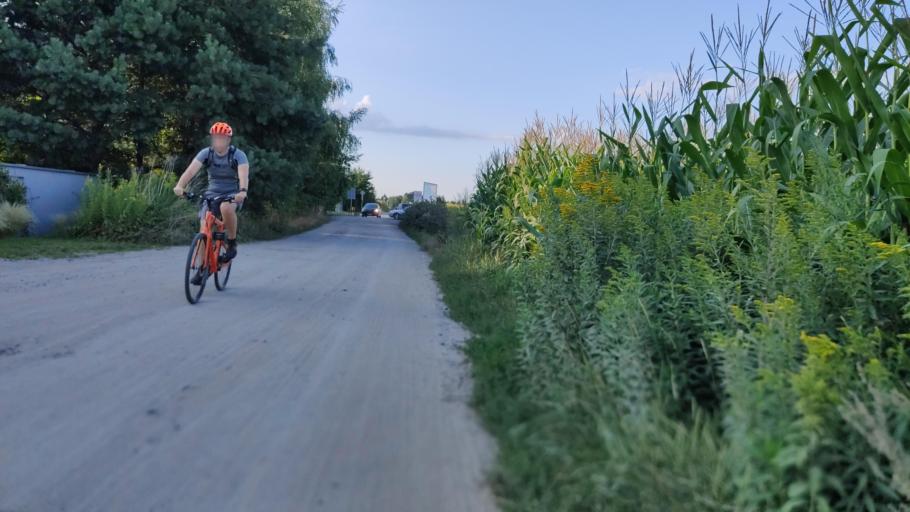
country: PL
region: Lower Silesian Voivodeship
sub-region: Powiat wroclawski
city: Zerniki Wroclawskie
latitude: 51.0497
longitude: 17.0658
